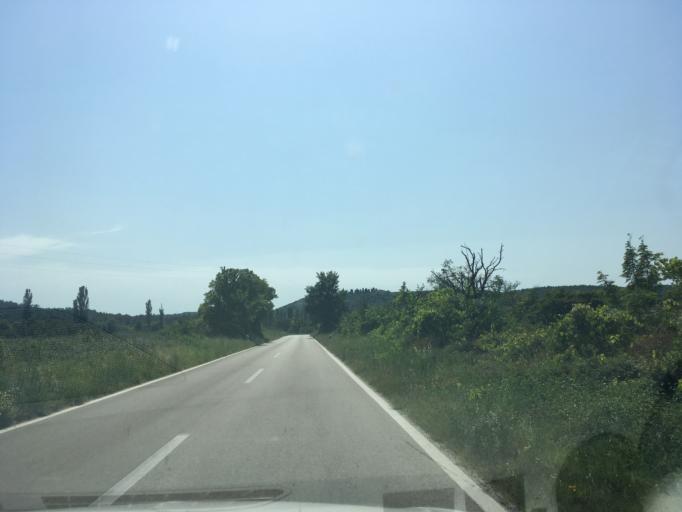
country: HR
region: Sibensko-Kniniska
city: Zaton
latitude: 43.9313
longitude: 15.8254
